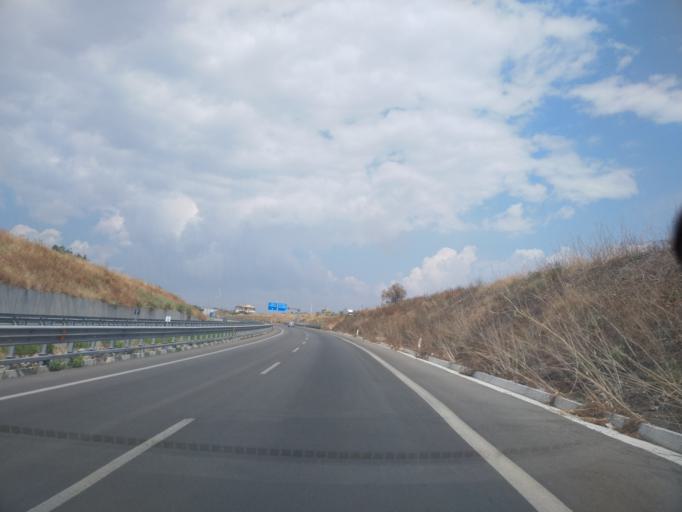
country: IT
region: Sicily
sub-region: Agrigento
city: Favara
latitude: 37.3502
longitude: 13.6769
